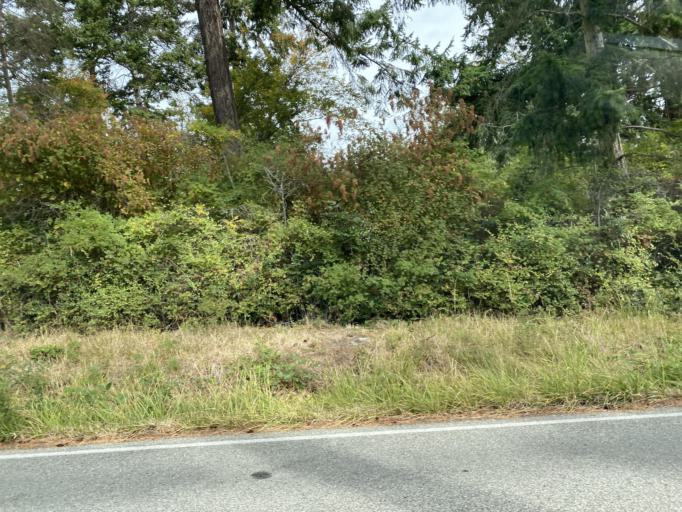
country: US
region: Washington
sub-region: Island County
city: Coupeville
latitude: 48.2391
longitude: -122.6897
